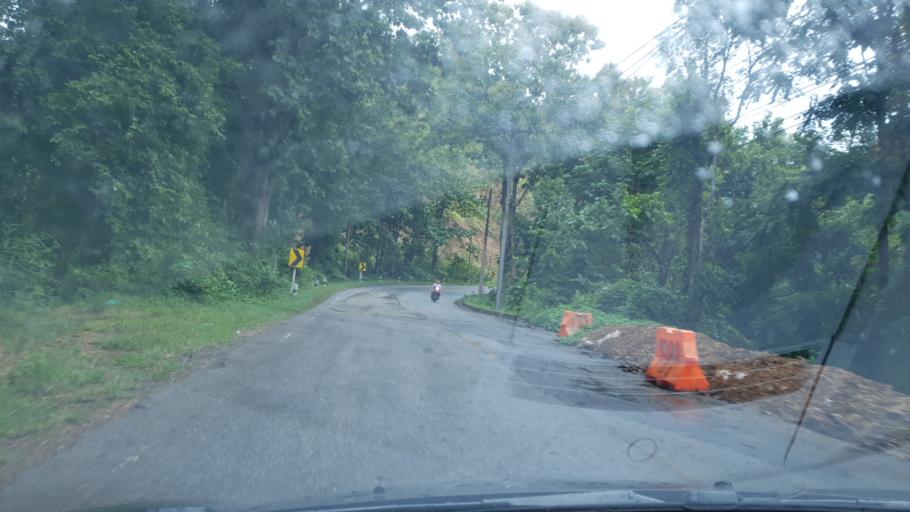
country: TH
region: Mae Hong Son
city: Pa Pae
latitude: 18.2811
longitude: 97.9379
